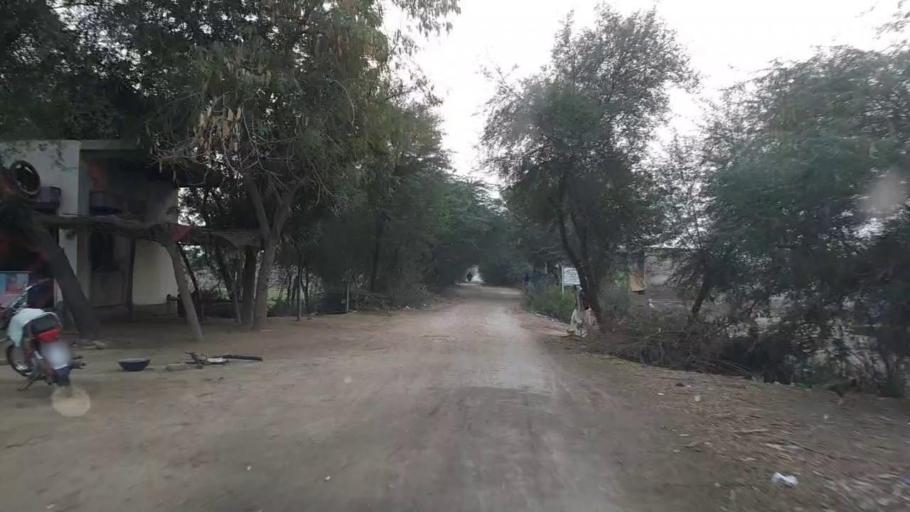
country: PK
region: Sindh
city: Kandiari
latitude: 26.9667
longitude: 68.4693
